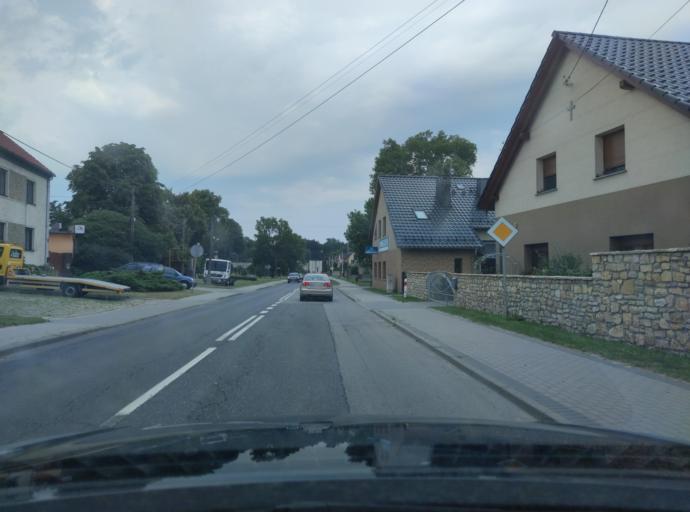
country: PL
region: Opole Voivodeship
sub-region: Powiat strzelecki
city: Strzelce Opolskie
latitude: 50.5047
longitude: 18.2944
